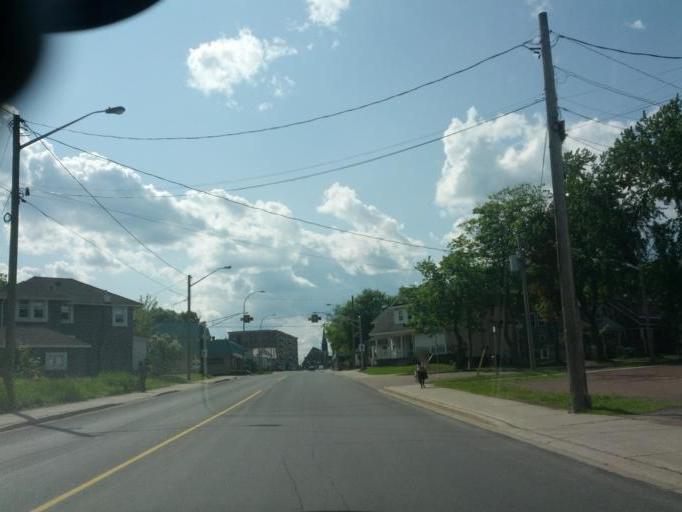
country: CA
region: New Brunswick
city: Moncton
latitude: 46.0957
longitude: -64.7893
